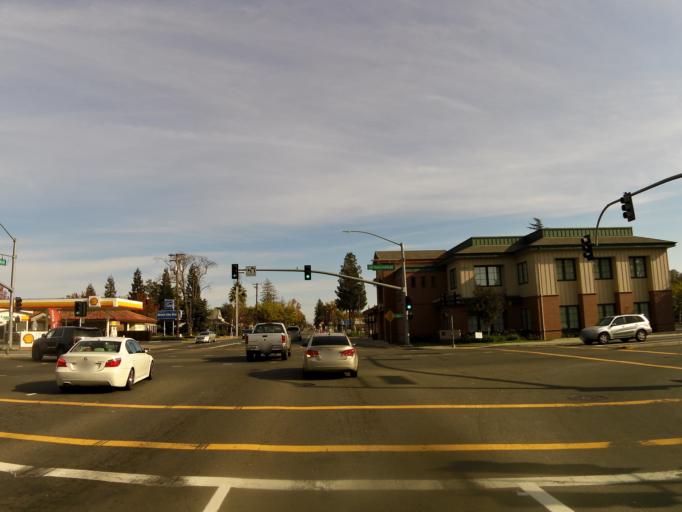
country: US
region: California
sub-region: Sacramento County
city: Elk Grove
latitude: 38.4090
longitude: -121.3719
